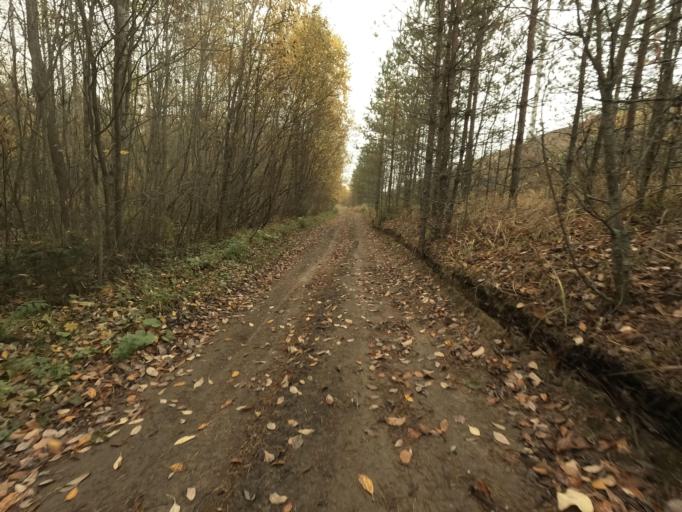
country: RU
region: Leningrad
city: Pavlovo
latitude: 59.7753
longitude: 30.9018
